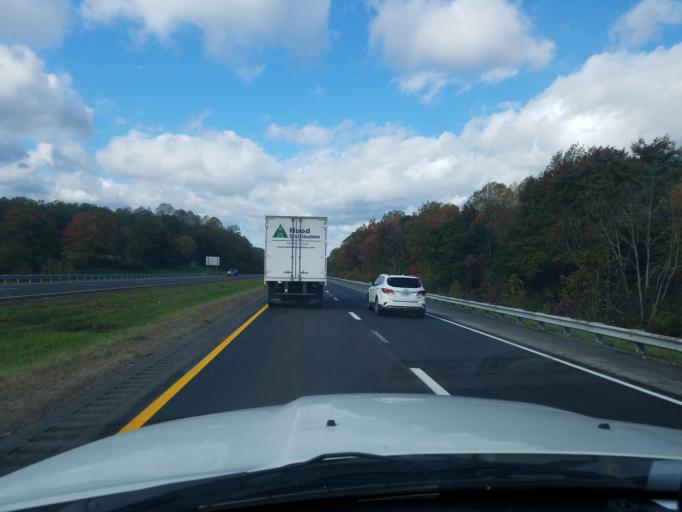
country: US
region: Kentucky
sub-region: Russell County
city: Russell Springs
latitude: 37.0449
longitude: -85.1058
